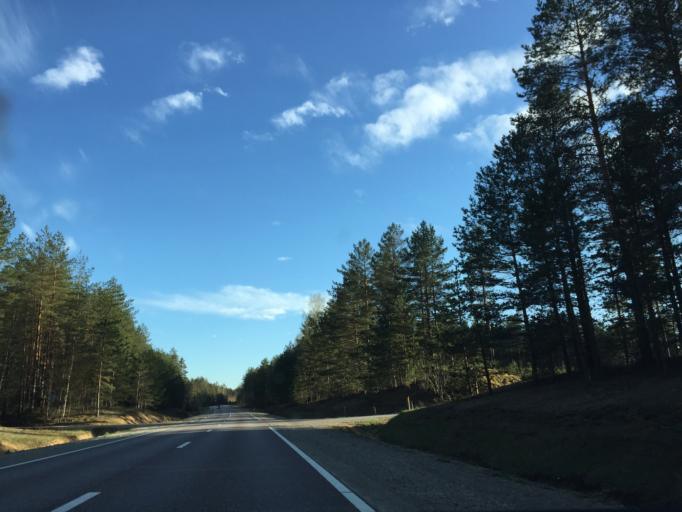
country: LV
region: Strenci
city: Seda
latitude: 57.6650
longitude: 25.8746
